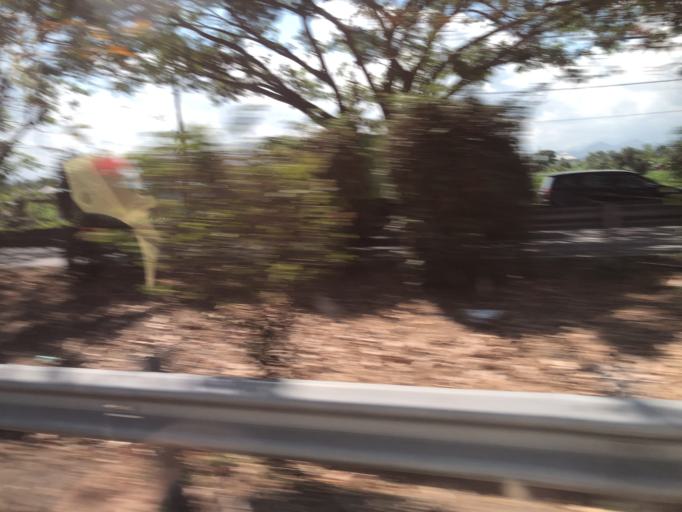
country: ID
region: Bali
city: Semarapura
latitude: -8.5695
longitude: 115.4044
